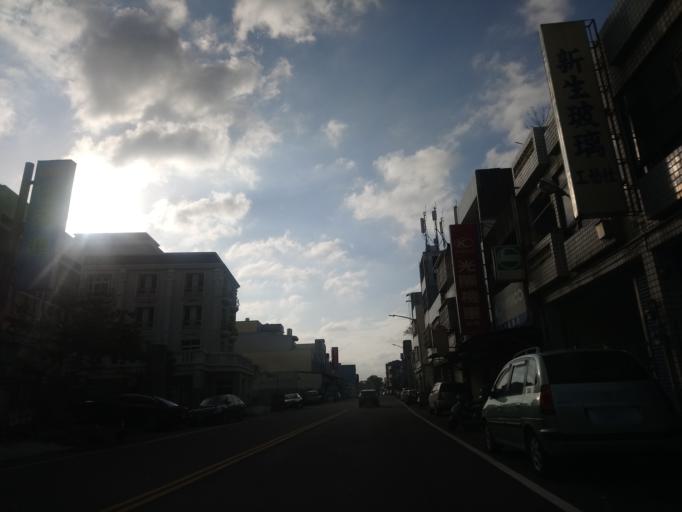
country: TW
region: Taiwan
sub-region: Hsinchu
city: Hsinchu
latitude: 24.8002
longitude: 120.9484
